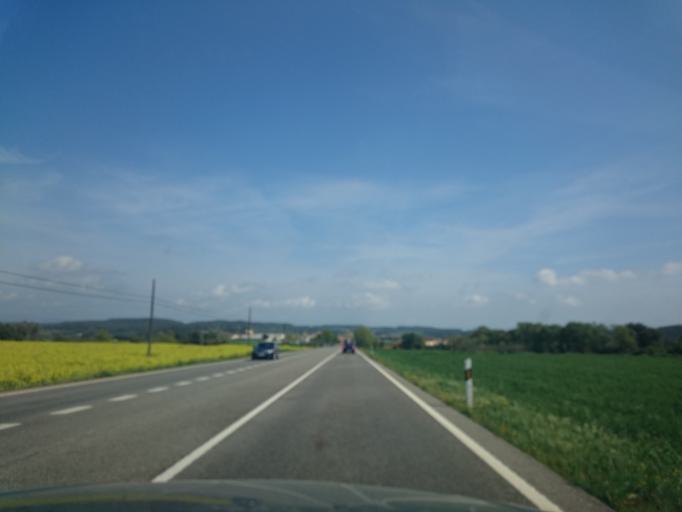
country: ES
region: Catalonia
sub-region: Provincia de Girona
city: Bascara
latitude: 42.1505
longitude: 2.9085
